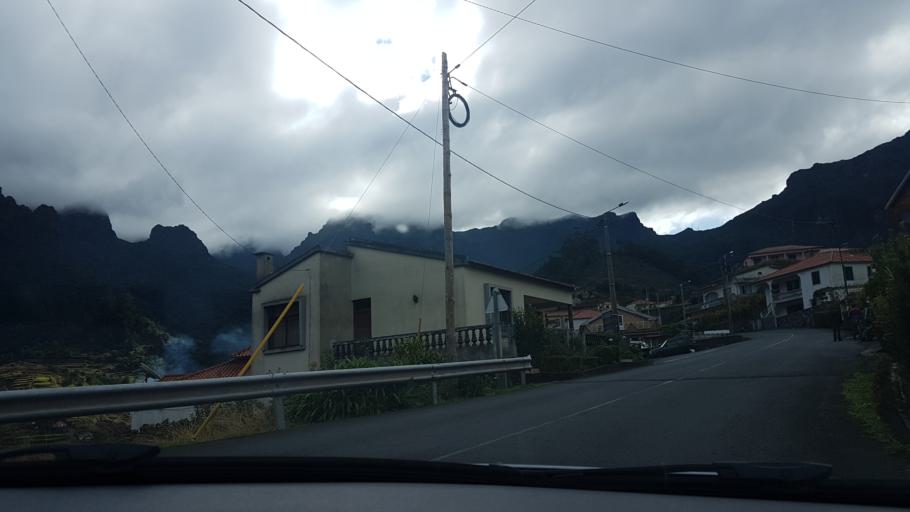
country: PT
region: Madeira
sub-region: Sao Vicente
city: Sao Vicente
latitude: 32.7822
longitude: -17.0304
